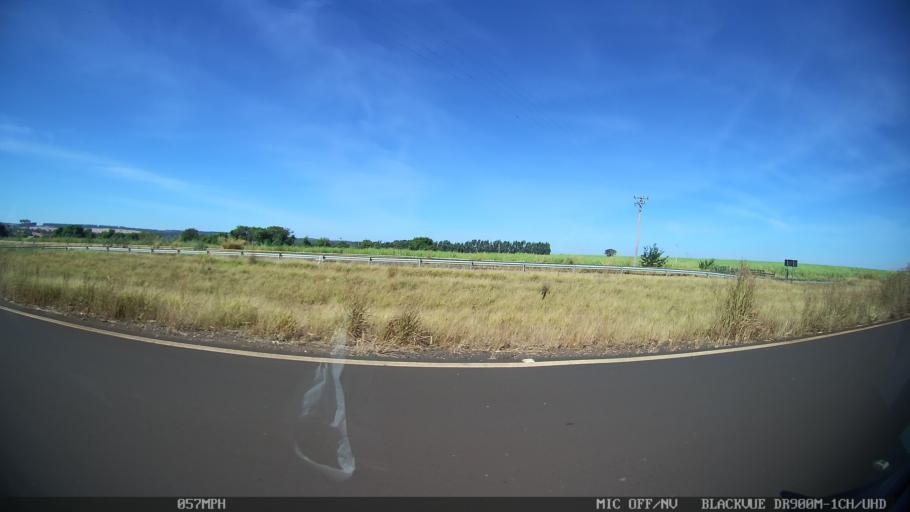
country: BR
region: Sao Paulo
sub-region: Franca
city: Franca
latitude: -20.5567
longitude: -47.4985
